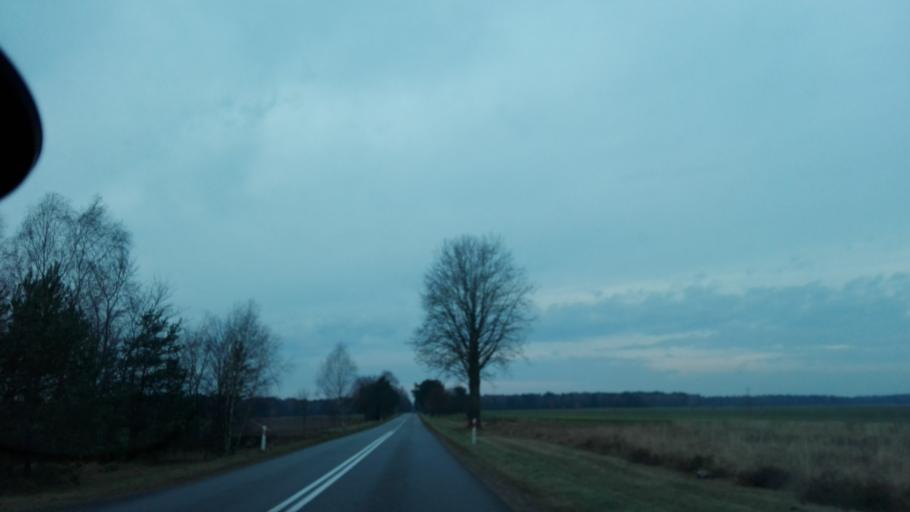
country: PL
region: Lublin Voivodeship
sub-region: Powiat radzynski
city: Komarowka Podlaska
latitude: 51.7766
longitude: 22.9140
